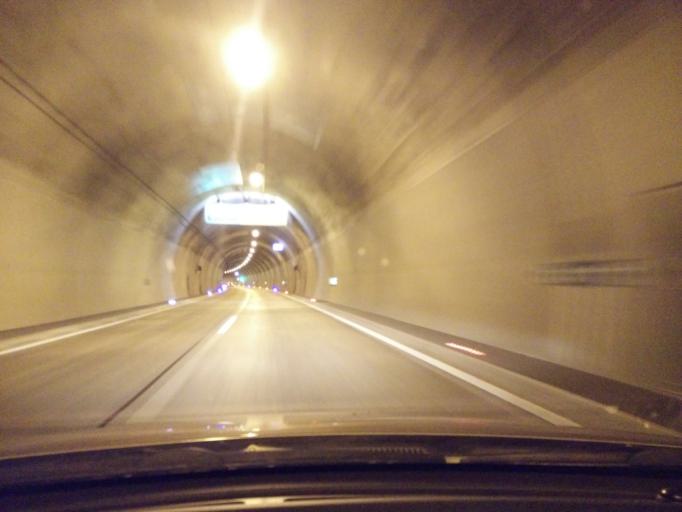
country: IT
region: Friuli Venezia Giulia
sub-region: Provincia di Trieste
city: Dolina
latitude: 45.5847
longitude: 13.8986
